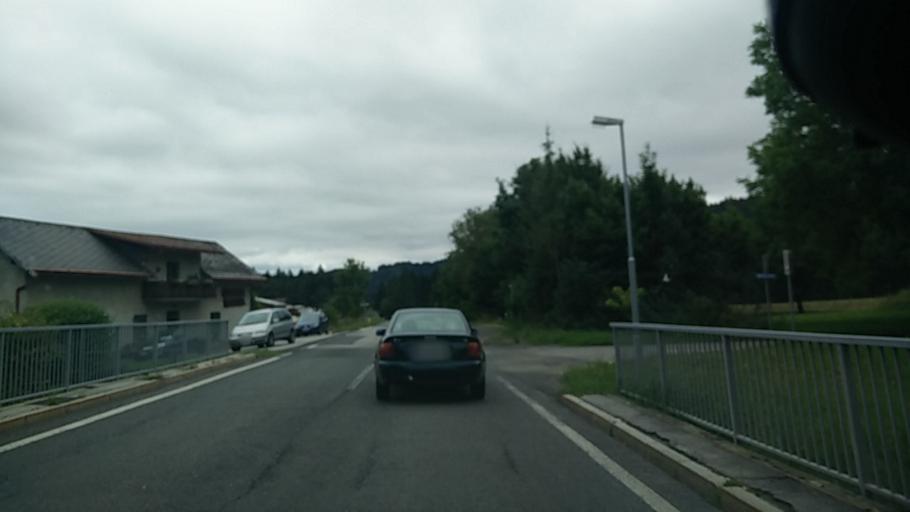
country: AT
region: Carinthia
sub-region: Politischer Bezirk Villach Land
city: Rosegg
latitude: 46.5522
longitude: 13.9928
